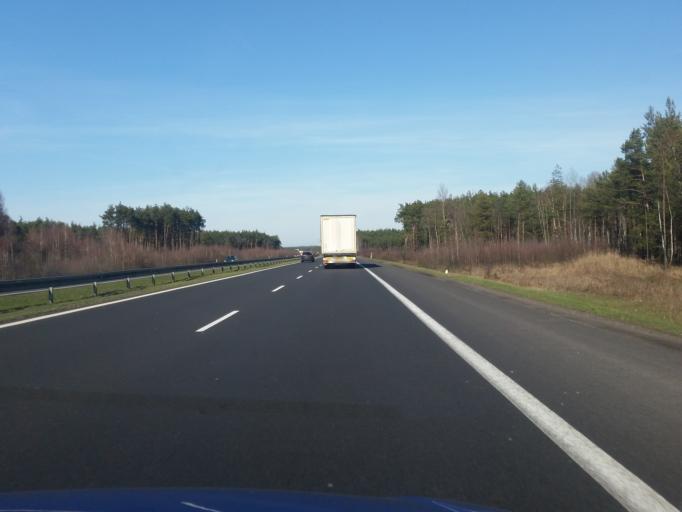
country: PL
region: Lodz Voivodeship
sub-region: Powiat radomszczanski
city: Radomsko
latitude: 51.0346
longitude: 19.3367
